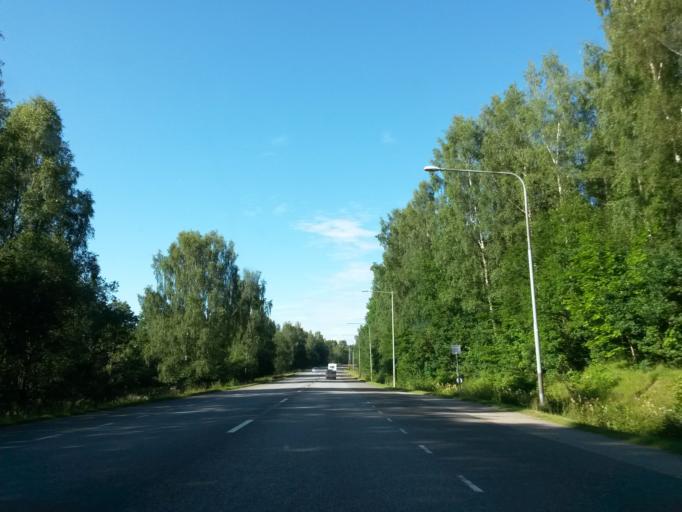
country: SE
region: Vaestra Goetaland
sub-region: Boras Kommun
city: Boras
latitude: 57.7697
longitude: 12.9736
